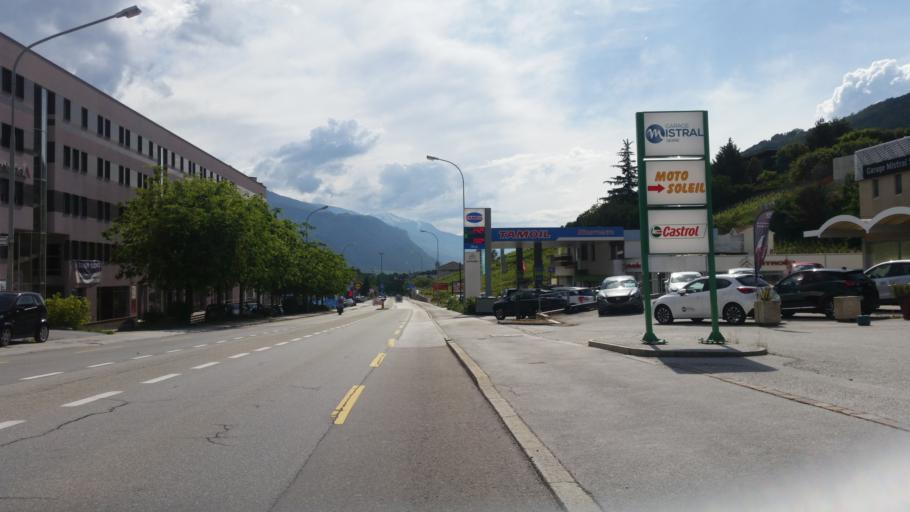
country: CH
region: Valais
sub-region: Sierre District
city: Sierre
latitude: 46.2860
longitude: 7.5184
